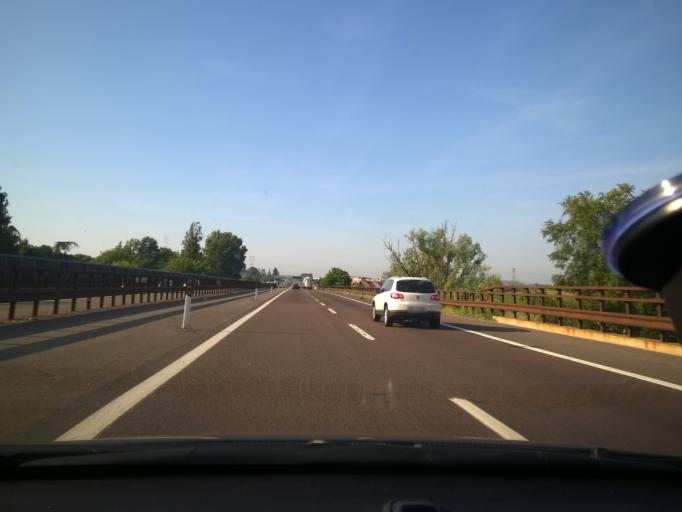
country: IT
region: Emilia-Romagna
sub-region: Provincia di Reggio Emilia
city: Rolo
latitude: 44.8863
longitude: 10.8503
